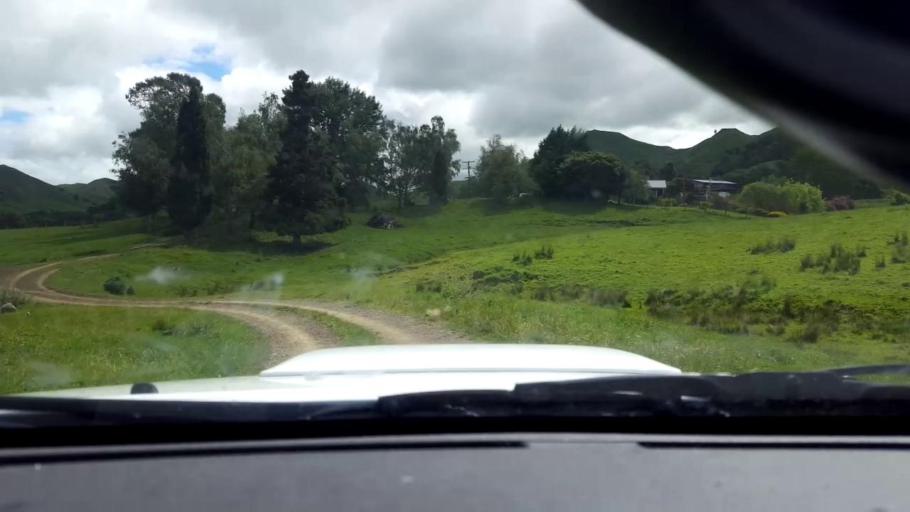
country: NZ
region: Gisborne
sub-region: Gisborne District
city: Gisborne
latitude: -38.4941
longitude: 177.6698
